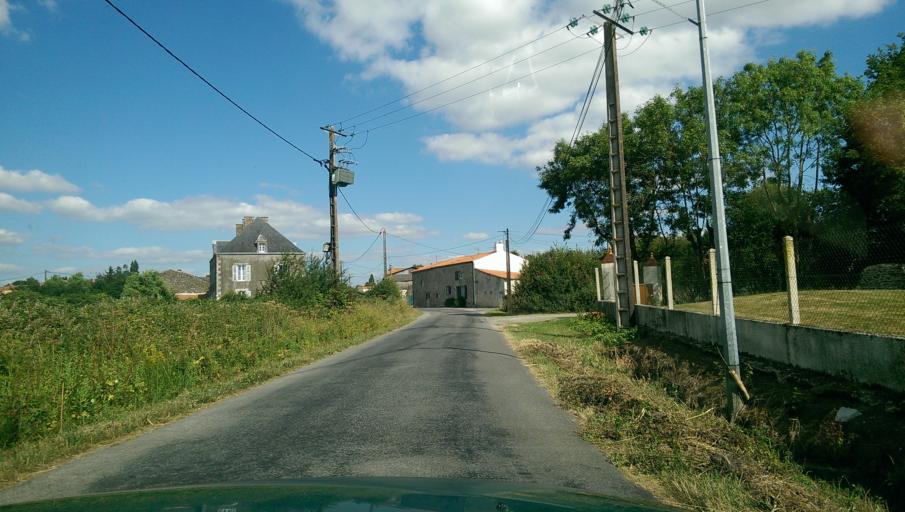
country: FR
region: Pays de la Loire
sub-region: Departement de la Loire-Atlantique
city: Lege
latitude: 46.9011
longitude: -1.5698
